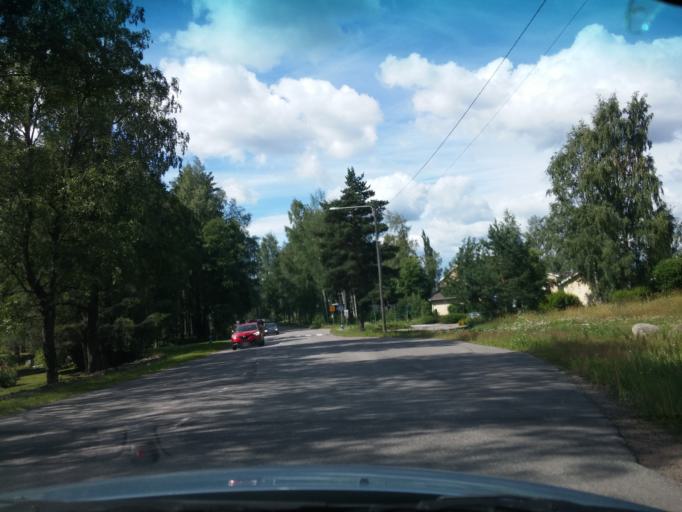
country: FI
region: Uusimaa
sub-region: Porvoo
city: Porvoo
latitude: 60.3927
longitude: 25.6425
